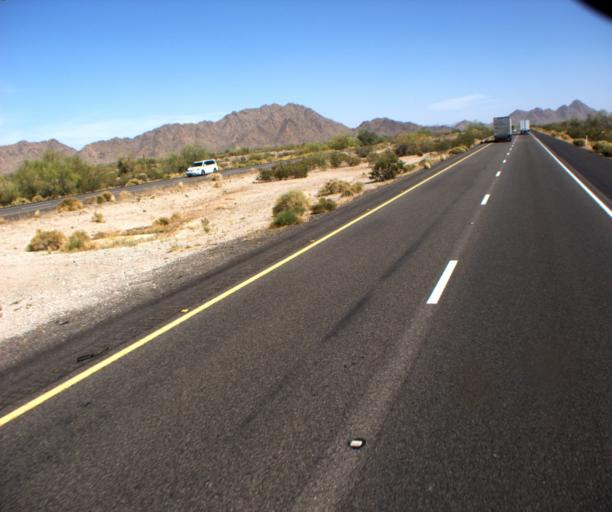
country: US
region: Arizona
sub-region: Maricopa County
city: Gila Bend
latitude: 32.9121
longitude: -112.6118
